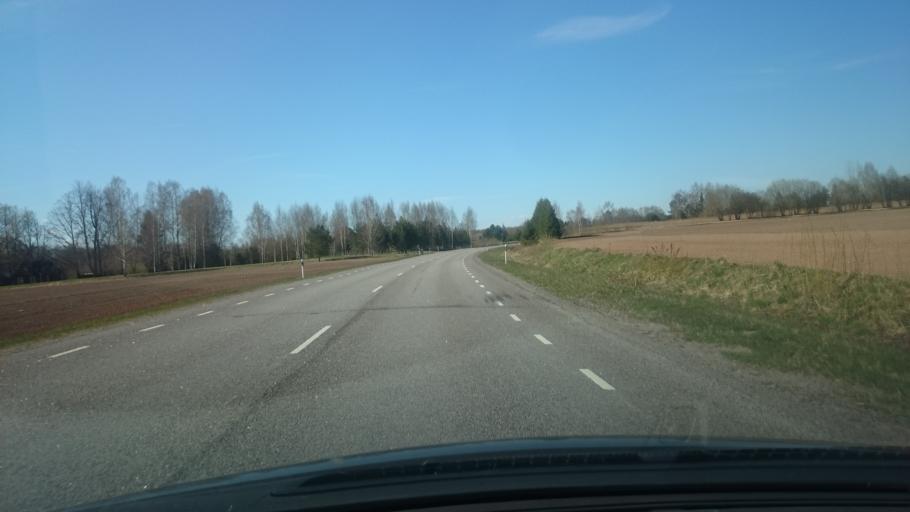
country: EE
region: Polvamaa
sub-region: Polva linn
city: Polva
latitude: 58.2463
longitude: 27.0040
